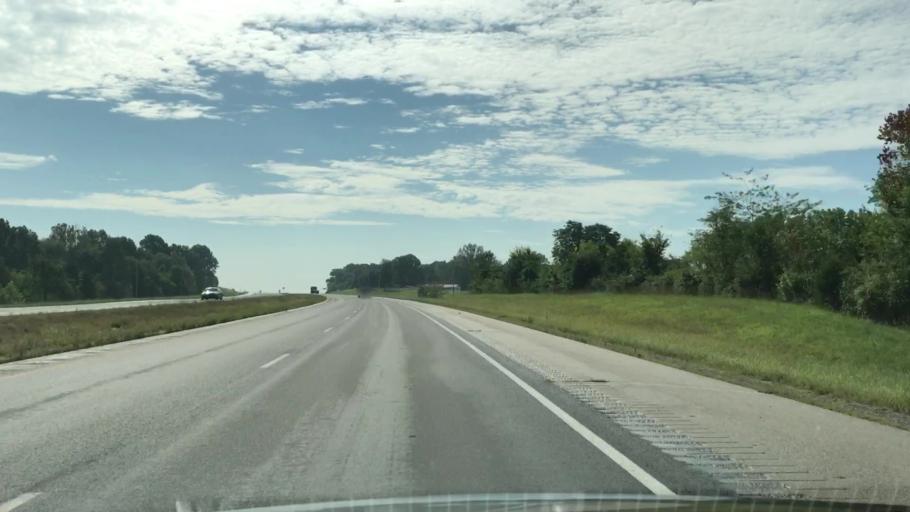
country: US
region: Kentucky
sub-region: Warren County
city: Plano
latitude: 36.8632
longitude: -86.3489
